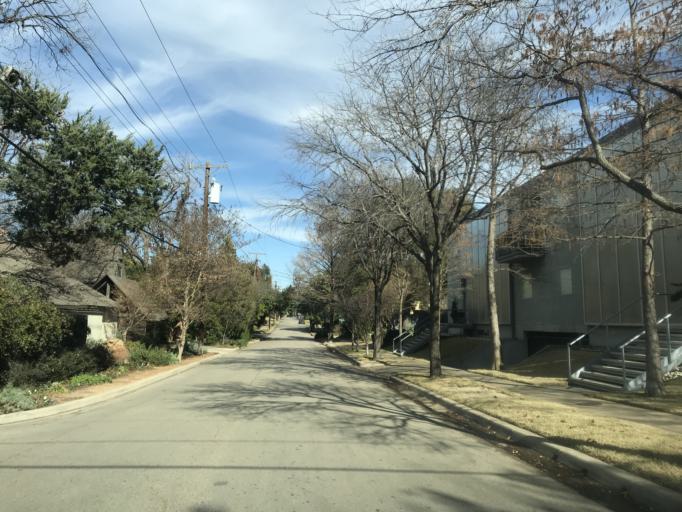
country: US
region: Texas
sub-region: Dallas County
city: Highland Park
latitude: 32.8199
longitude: -96.7956
